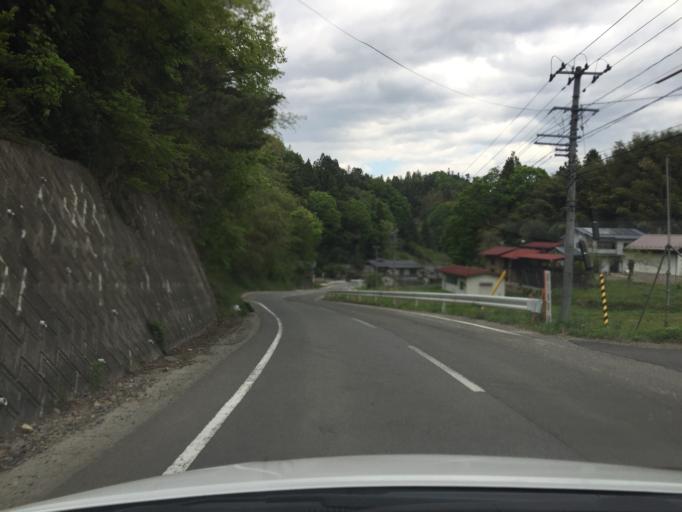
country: JP
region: Fukushima
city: Yanagawamachi-saiwaicho
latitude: 37.7472
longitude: 140.6395
